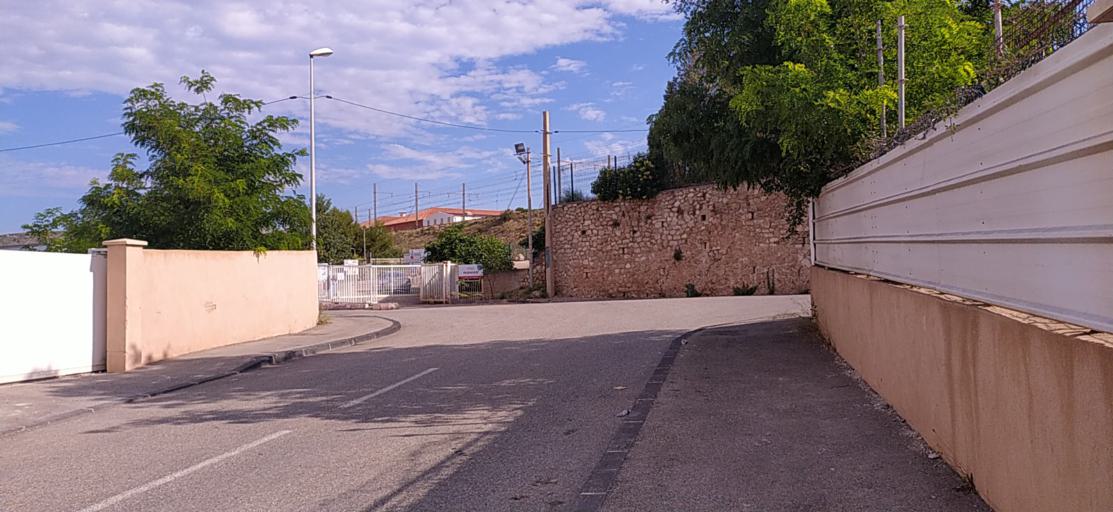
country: FR
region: Provence-Alpes-Cote d'Azur
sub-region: Departement des Bouches-du-Rhone
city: Marseille 16
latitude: 43.3549
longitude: 5.3502
